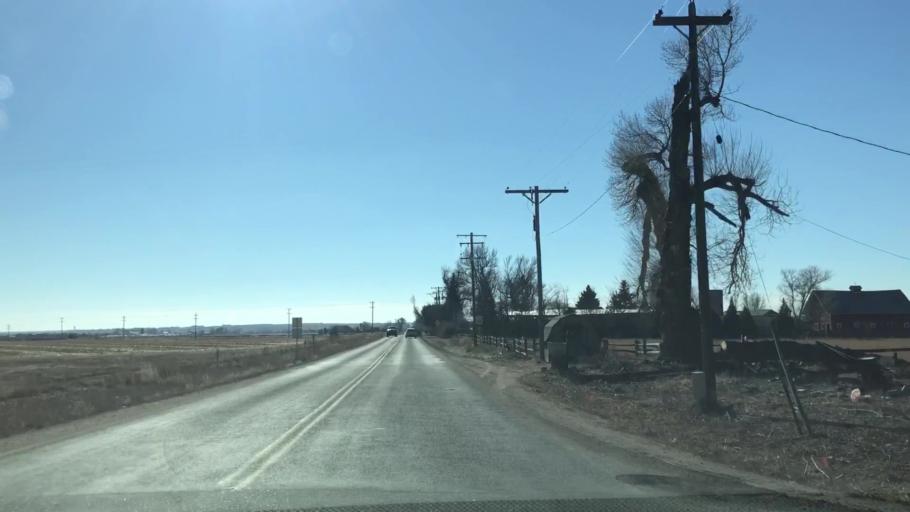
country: US
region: Colorado
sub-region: Weld County
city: Windsor
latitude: 40.5081
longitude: -104.9442
